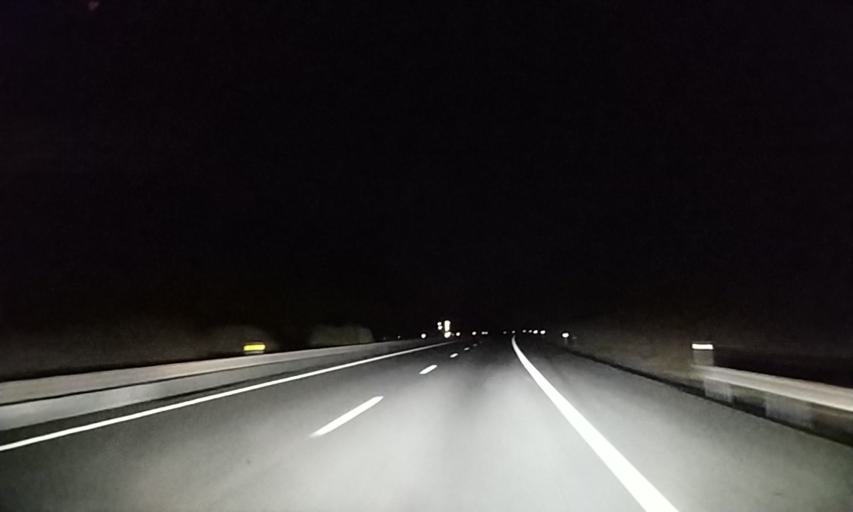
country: PT
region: Aveiro
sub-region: Aveiro
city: Eixo
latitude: 40.6440
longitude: -8.5217
